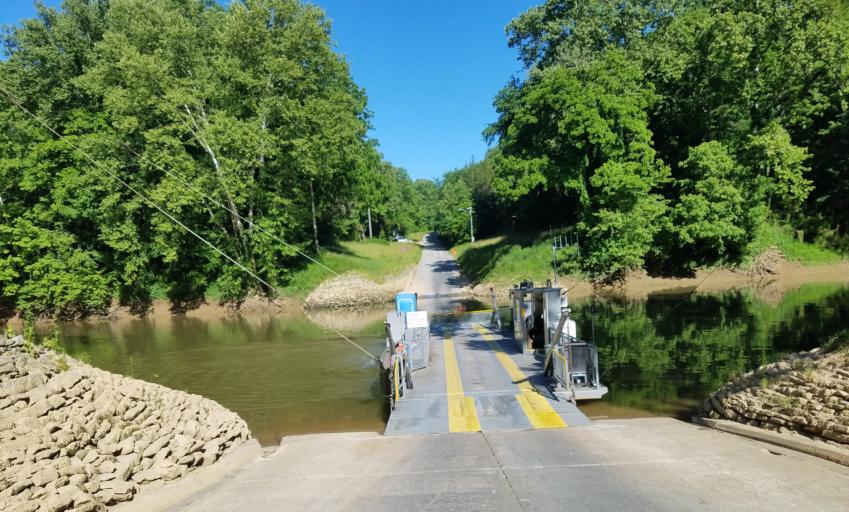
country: US
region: Kentucky
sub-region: Edmonson County
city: Brownsville
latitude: 37.1794
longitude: -86.1118
